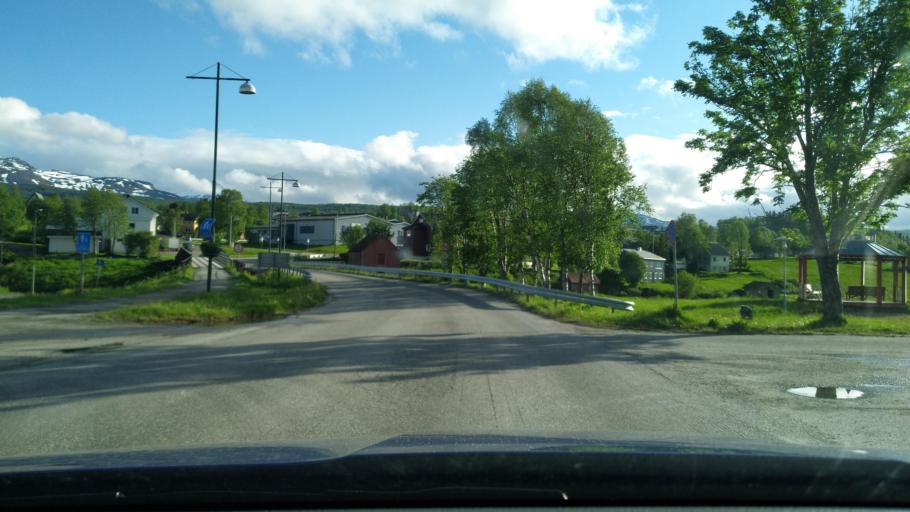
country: NO
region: Troms
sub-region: Sorreisa
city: Sorreisa
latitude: 69.1448
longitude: 18.1514
